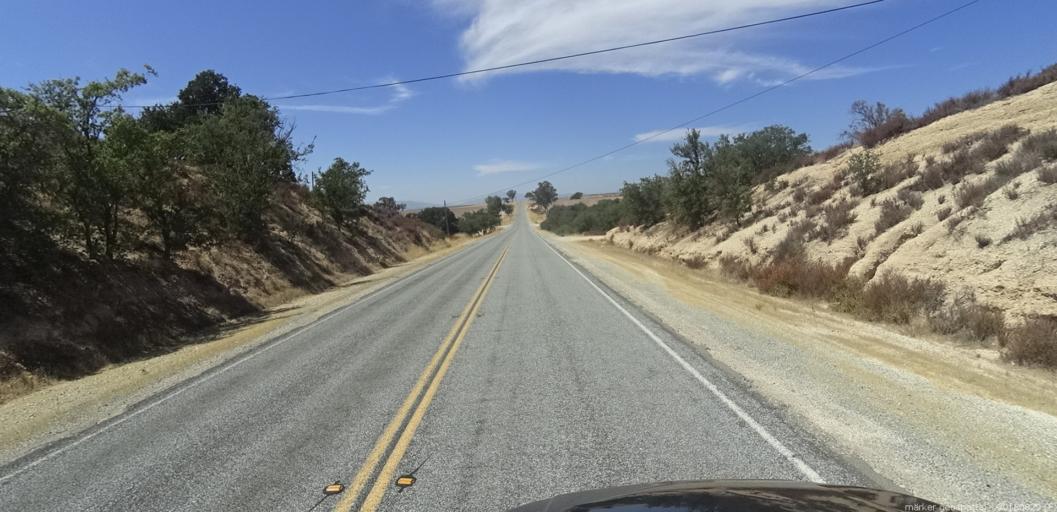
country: US
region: California
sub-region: San Luis Obispo County
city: Lake Nacimiento
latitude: 35.9166
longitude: -121.0283
